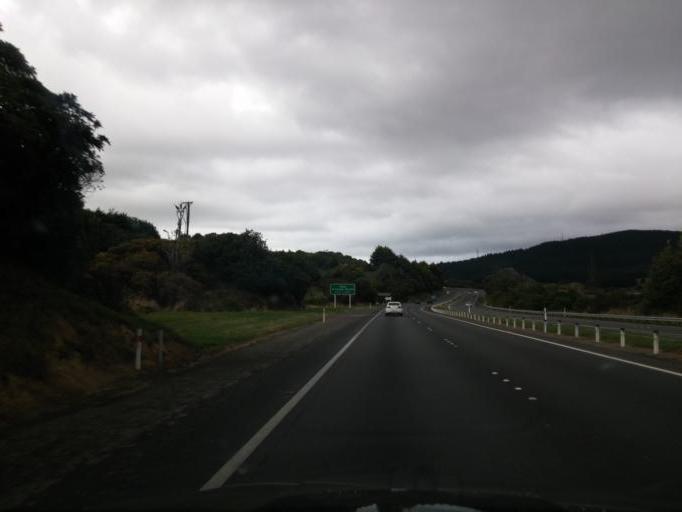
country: NZ
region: Wellington
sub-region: Porirua City
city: Porirua
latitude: -41.1757
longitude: 174.8304
